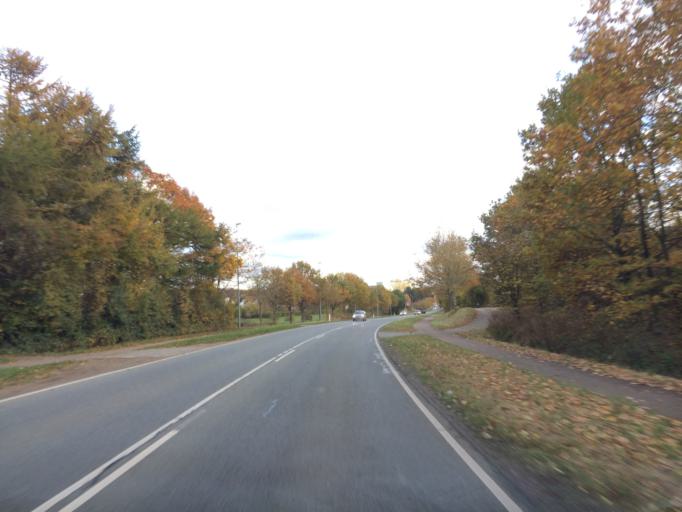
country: DK
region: South Denmark
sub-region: Sonderborg Kommune
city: Nordborg
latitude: 55.0402
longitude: 9.8027
